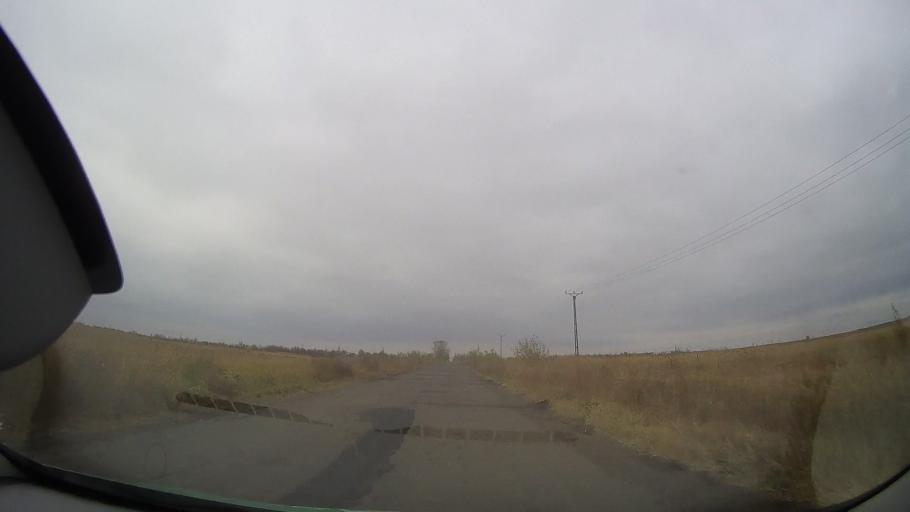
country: RO
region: Braila
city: Dudesti
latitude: 44.9360
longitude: 27.4257
